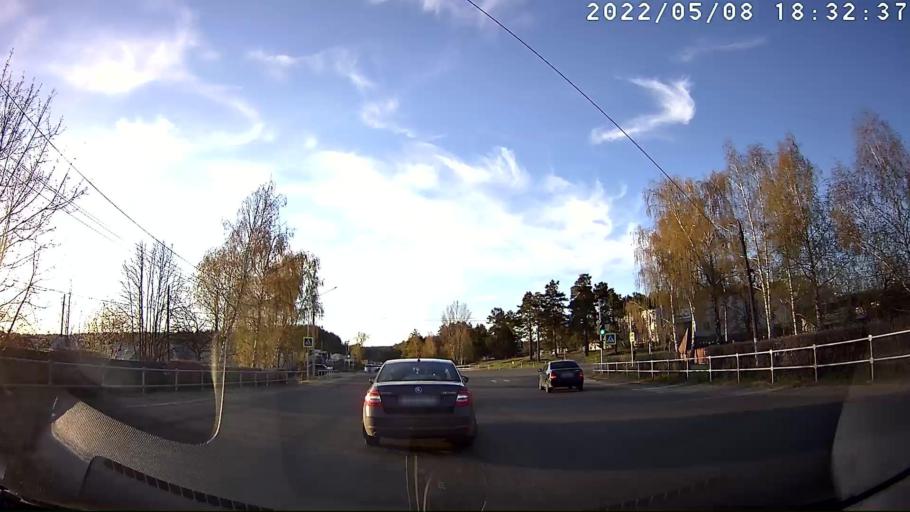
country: RU
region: Mariy-El
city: Volzhsk
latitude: 55.8865
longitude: 48.3597
